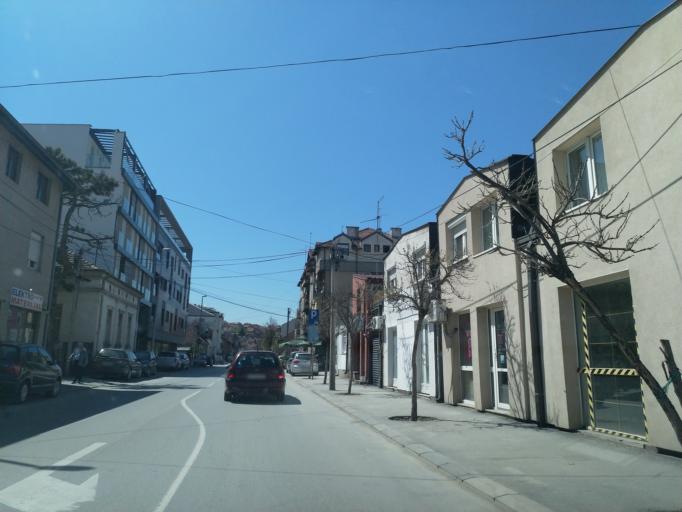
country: RS
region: Central Serbia
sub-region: Kolubarski Okrug
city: Valjevo
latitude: 44.2722
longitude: 19.8836
